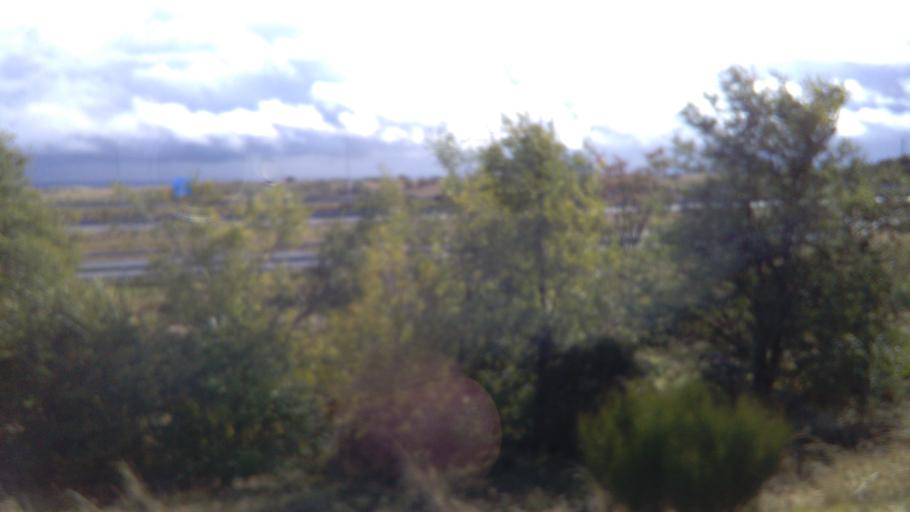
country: ES
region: Madrid
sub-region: Provincia de Madrid
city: Navalcarnero
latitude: 40.2654
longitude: -4.0406
